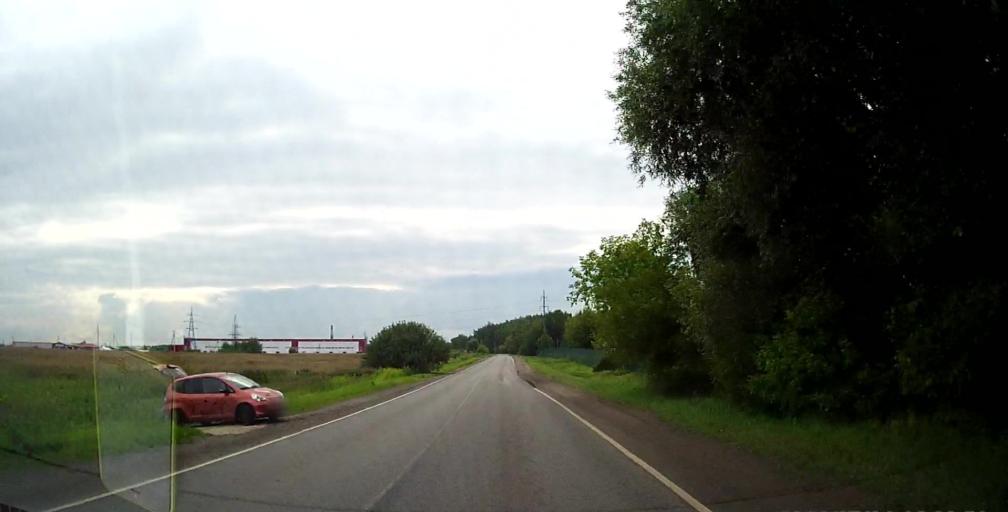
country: RU
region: Moskovskaya
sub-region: Podol'skiy Rayon
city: Podol'sk
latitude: 55.3892
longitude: 37.5784
